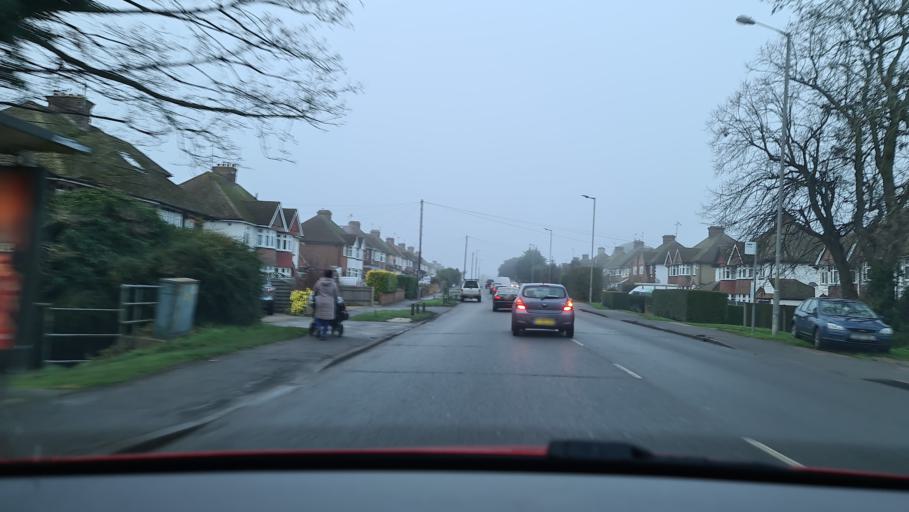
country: GB
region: England
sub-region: Buckinghamshire
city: Weston Turville
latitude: 51.8125
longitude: -0.7797
